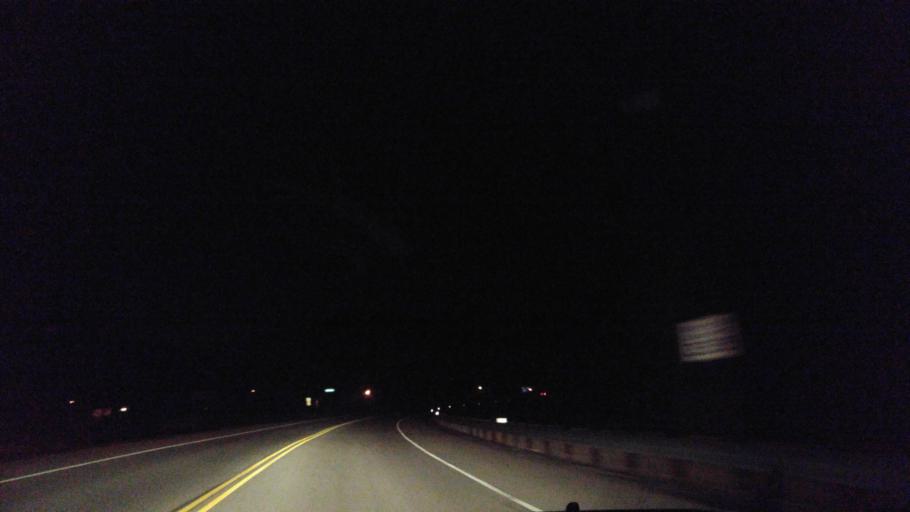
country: US
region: Ohio
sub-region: Athens County
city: Nelsonville
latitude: 39.4709
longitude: -82.2511
